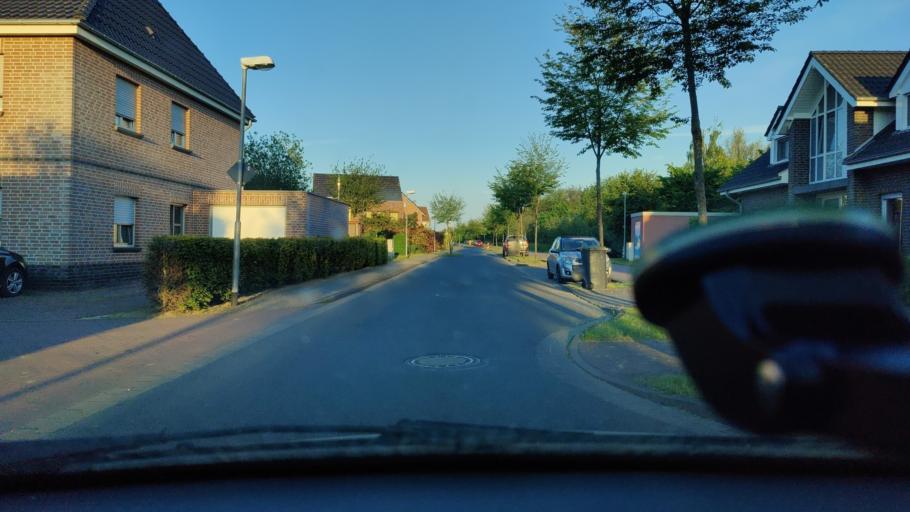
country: DE
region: North Rhine-Westphalia
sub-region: Regierungsbezirk Dusseldorf
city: Kranenburg
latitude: 51.7888
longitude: 6.0027
